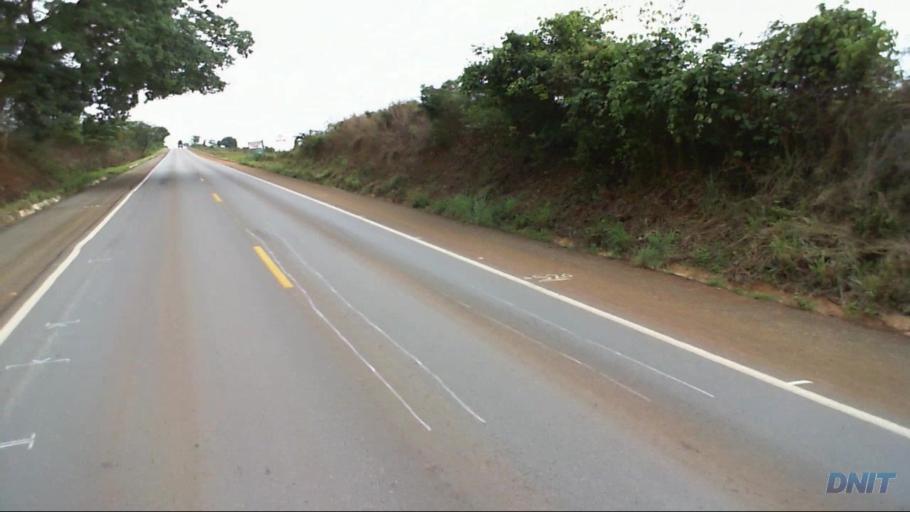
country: BR
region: Goias
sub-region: Uruacu
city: Uruacu
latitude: -14.6823
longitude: -49.1348
